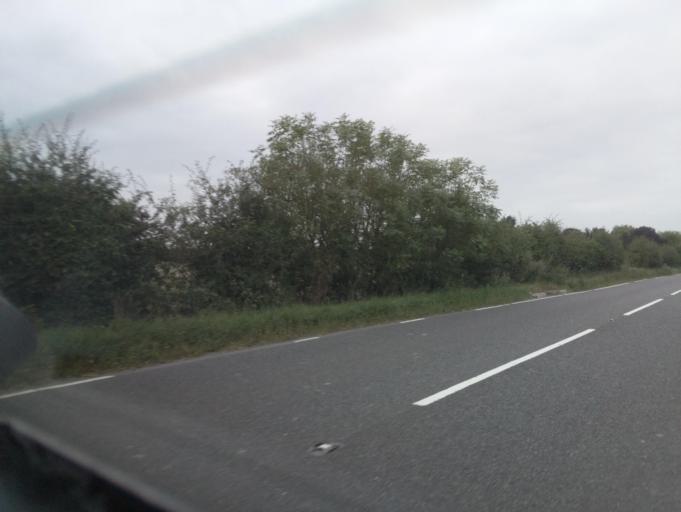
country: GB
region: England
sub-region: Shropshire
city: Astley
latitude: 52.7556
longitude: -2.6965
